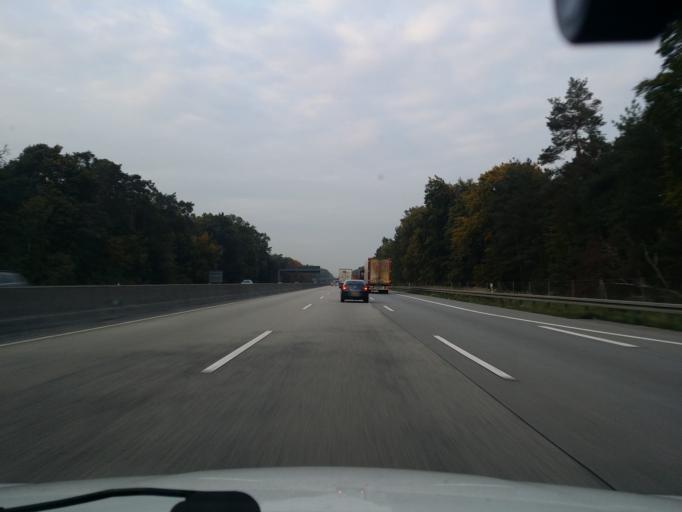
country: DE
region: Hesse
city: Viernheim
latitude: 49.5693
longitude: 8.5594
